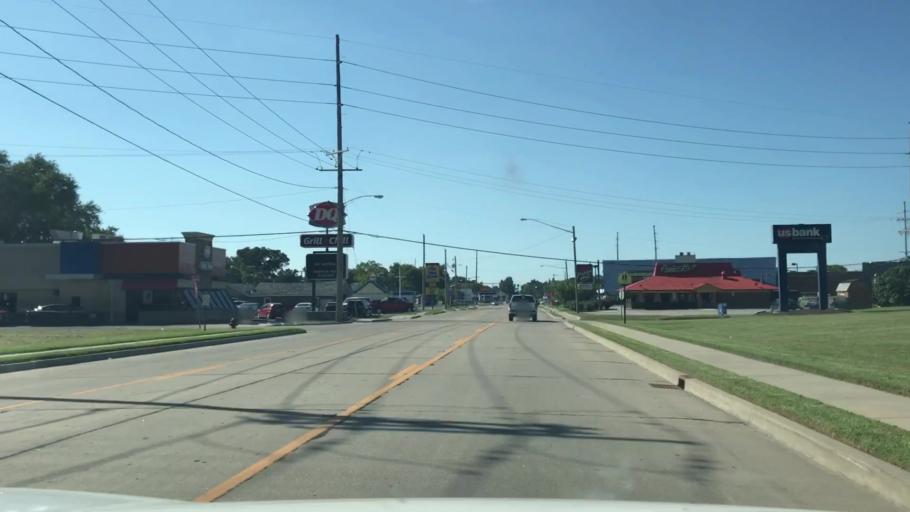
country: US
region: Illinois
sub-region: Madison County
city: Roxana
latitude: 38.8624
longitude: -90.0765
